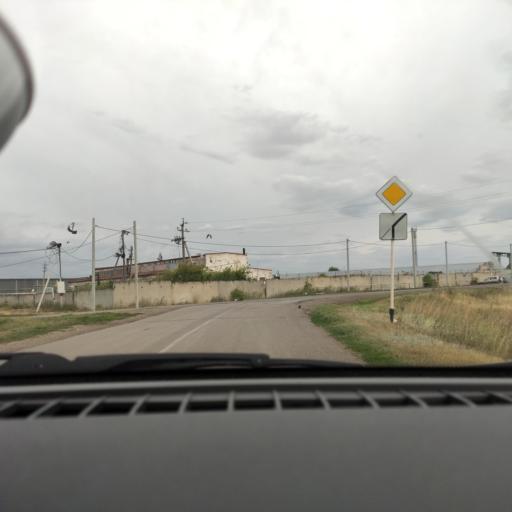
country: RU
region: Samara
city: Georgiyevka
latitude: 53.4723
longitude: 50.9409
